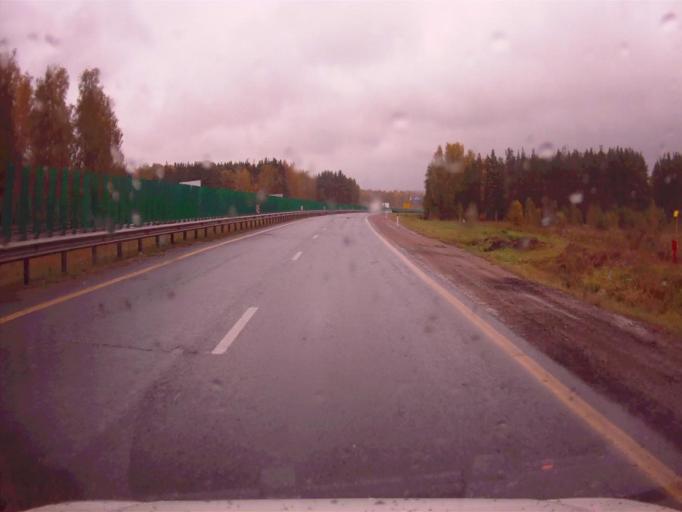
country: RU
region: Chelyabinsk
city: Dolgoderevenskoye
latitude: 55.3375
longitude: 61.3087
